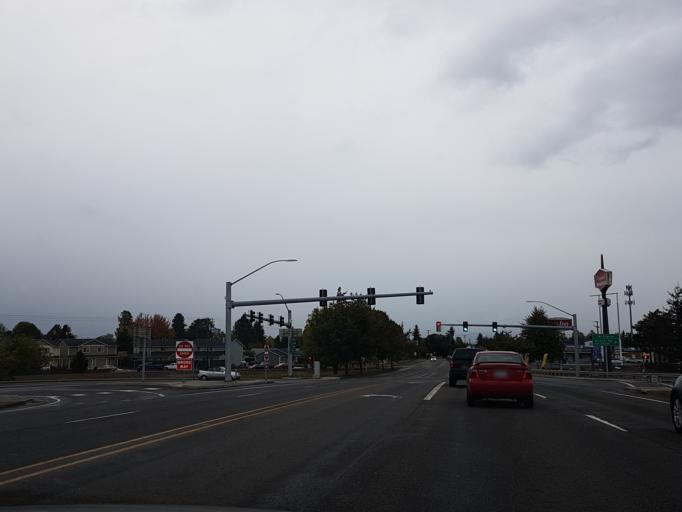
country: US
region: Oregon
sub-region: Linn County
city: Albany
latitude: 44.6302
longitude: -123.0630
